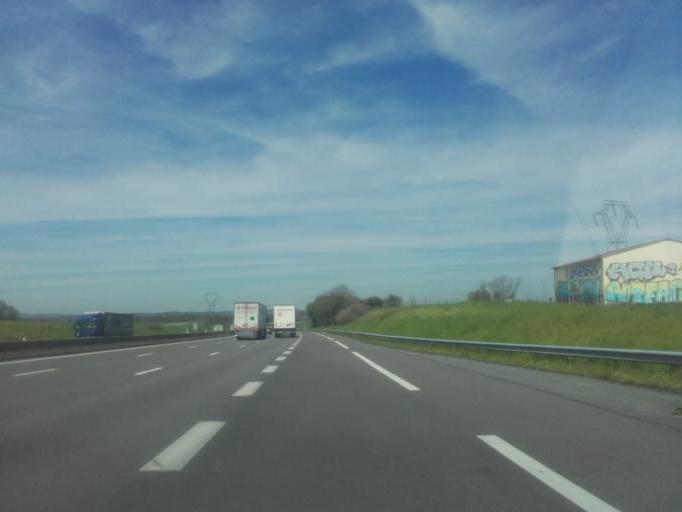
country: FR
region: Bourgogne
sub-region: Departement de Saone-et-Loire
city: Saint-Martin-Belle-Roche
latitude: 46.4237
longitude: 4.8674
